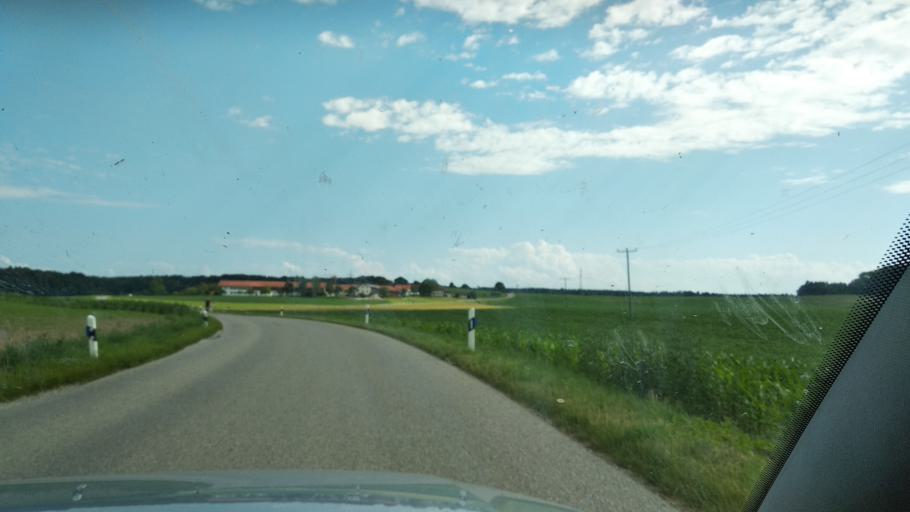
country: DE
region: Bavaria
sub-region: Upper Bavaria
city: Kirchseeon
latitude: 48.0578
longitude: 11.8976
